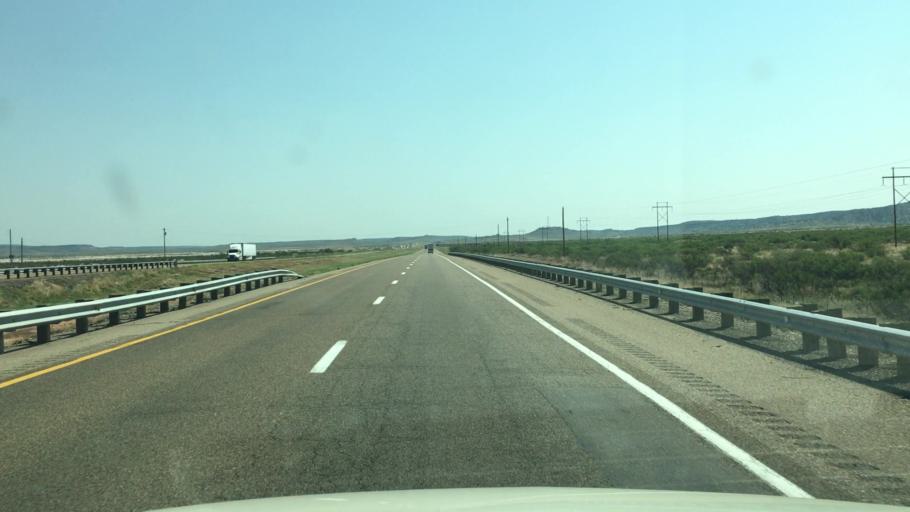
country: US
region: New Mexico
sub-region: Quay County
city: Tucumcari
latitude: 35.1123
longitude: -104.0022
